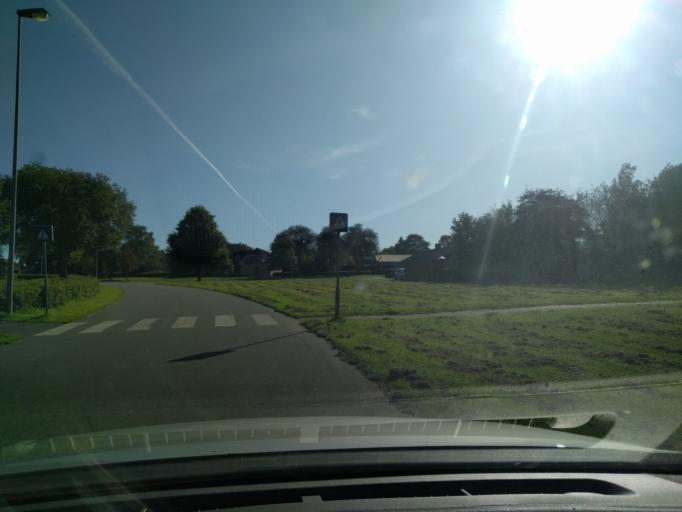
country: DK
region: Central Jutland
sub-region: Horsens Kommune
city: Horsens
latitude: 55.9329
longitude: 9.8496
